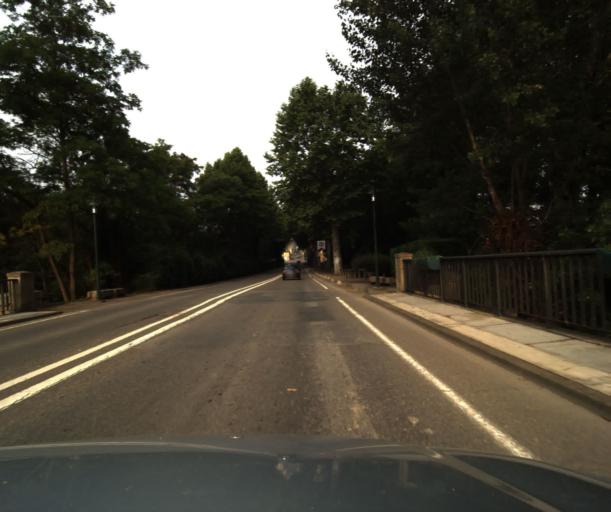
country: FR
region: Midi-Pyrenees
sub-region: Departement du Gers
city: Mirande
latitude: 43.5158
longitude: 0.4117
